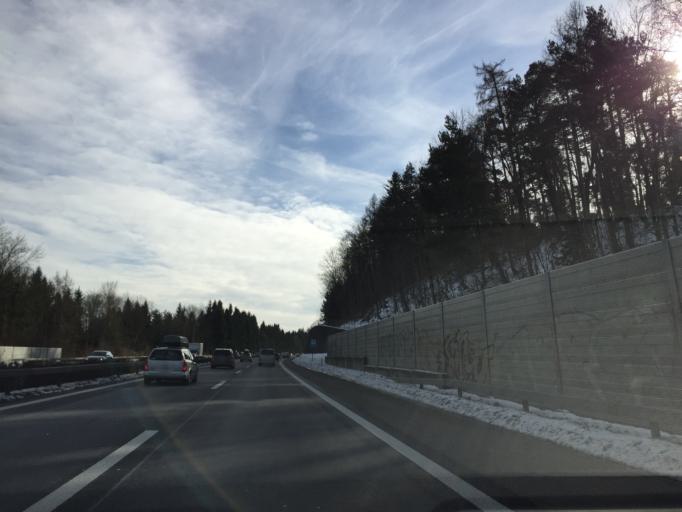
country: CH
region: Zurich
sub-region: Bezirk Horgen
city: Thalwil / Berg
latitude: 47.2850
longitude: 8.5567
